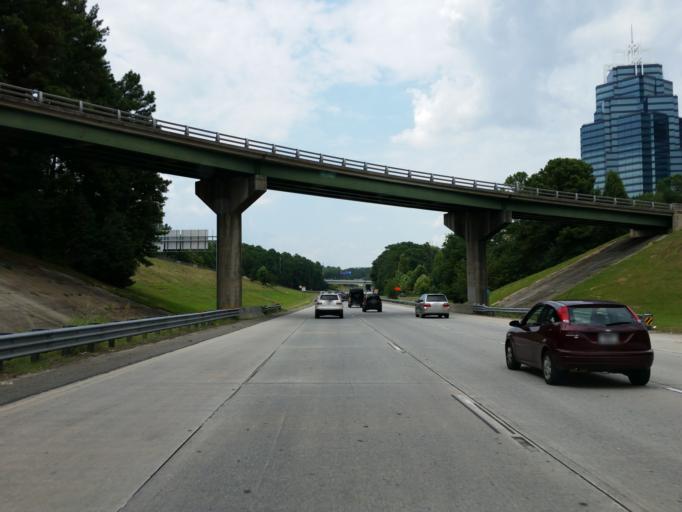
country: US
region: Georgia
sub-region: Fulton County
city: Sandy Springs
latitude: 33.9129
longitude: -84.3570
